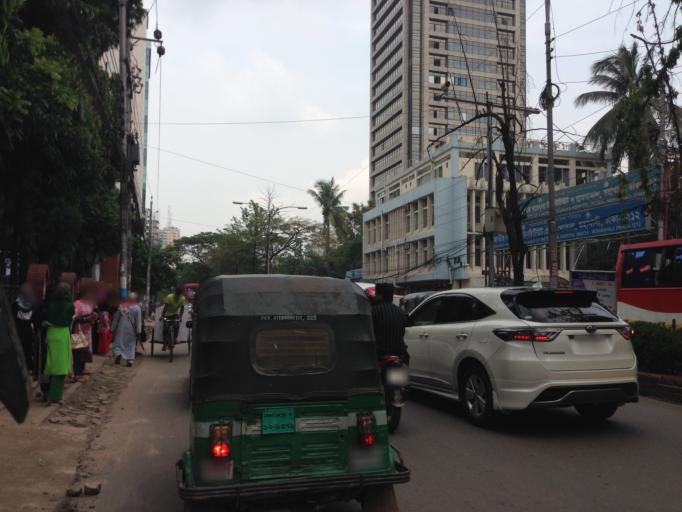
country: BD
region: Dhaka
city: Paltan
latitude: 23.7803
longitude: 90.4091
